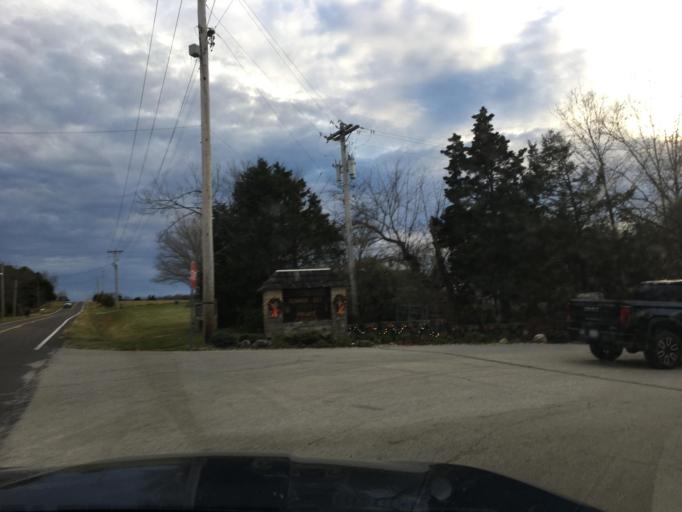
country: US
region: Missouri
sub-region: Jefferson County
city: De Soto
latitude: 38.0912
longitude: -90.5618
